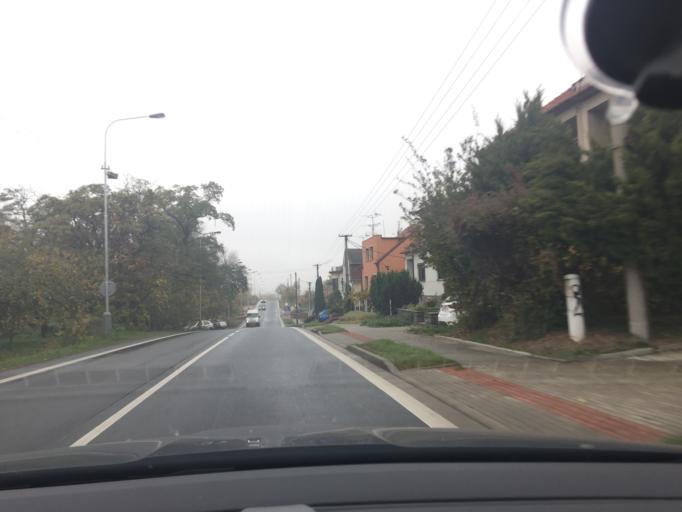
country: CZ
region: South Moravian
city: Rousinov
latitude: 49.1981
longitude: 16.8684
